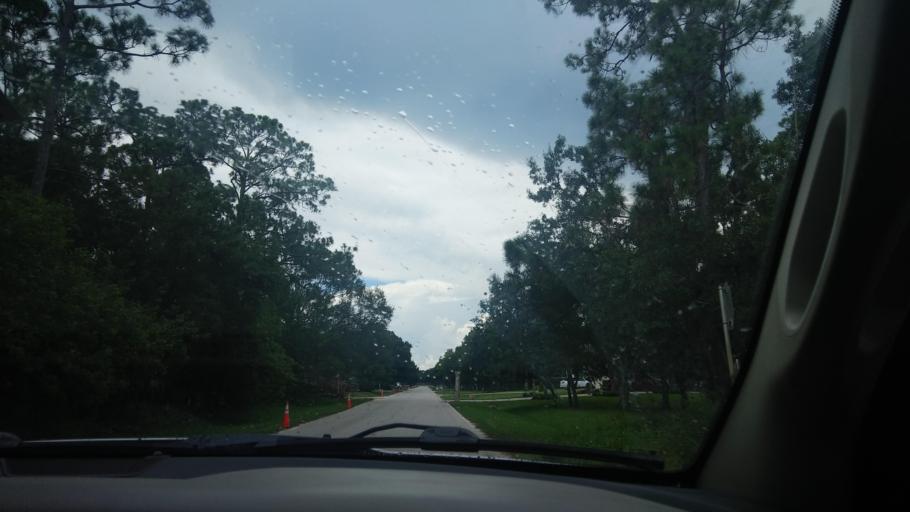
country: US
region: Florida
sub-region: Indian River County
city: Fellsmere
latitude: 27.7638
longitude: -80.6015
